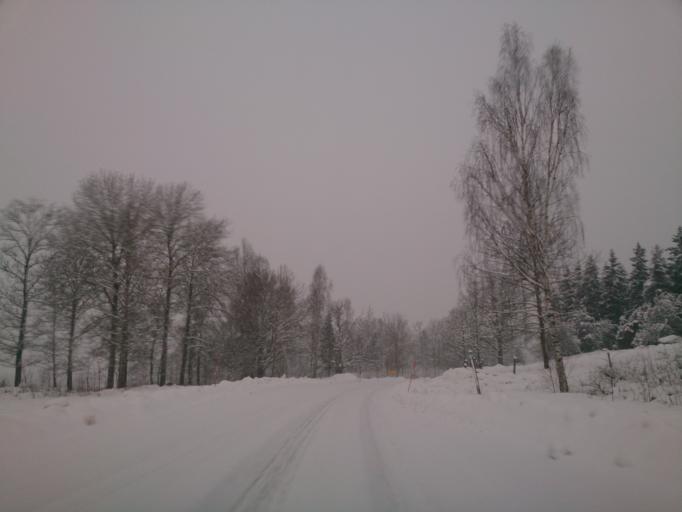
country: SE
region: OEstergoetland
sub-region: Atvidabergs Kommun
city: Atvidaberg
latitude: 58.3614
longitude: 16.0272
